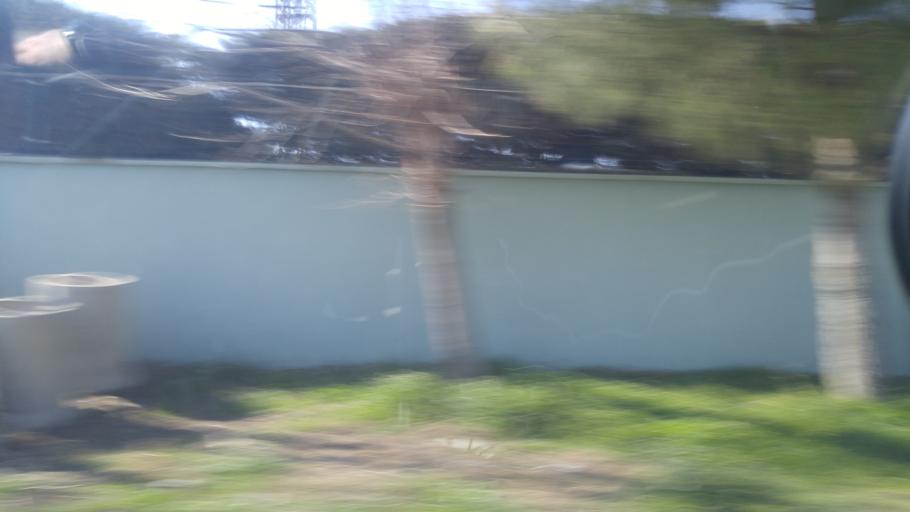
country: TR
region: Istanbul
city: Canta
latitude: 41.0835
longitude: 28.1076
